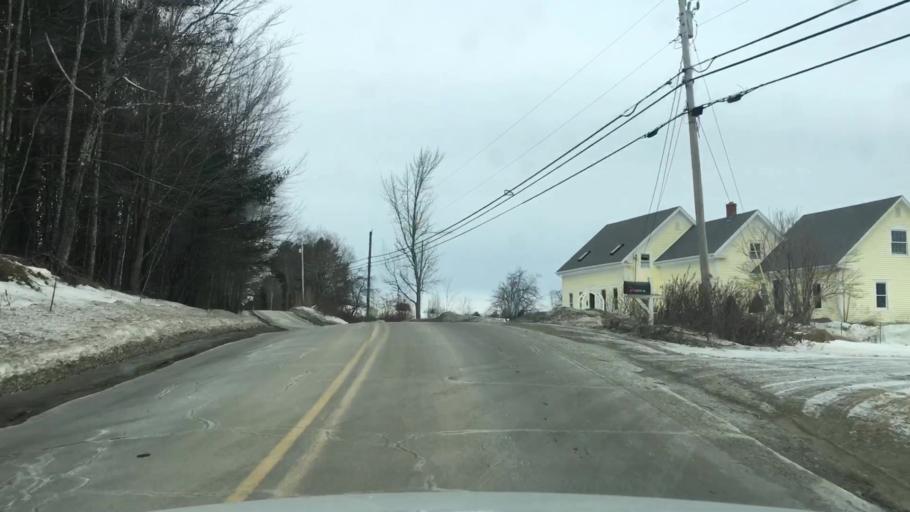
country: US
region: Maine
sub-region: Lincoln County
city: Whitefield
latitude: 44.2362
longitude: -69.6182
